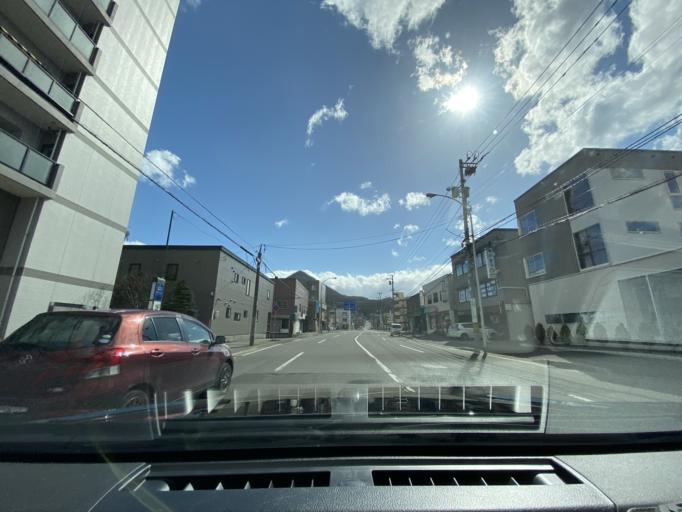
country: JP
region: Hokkaido
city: Sapporo
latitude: 43.0690
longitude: 141.2955
